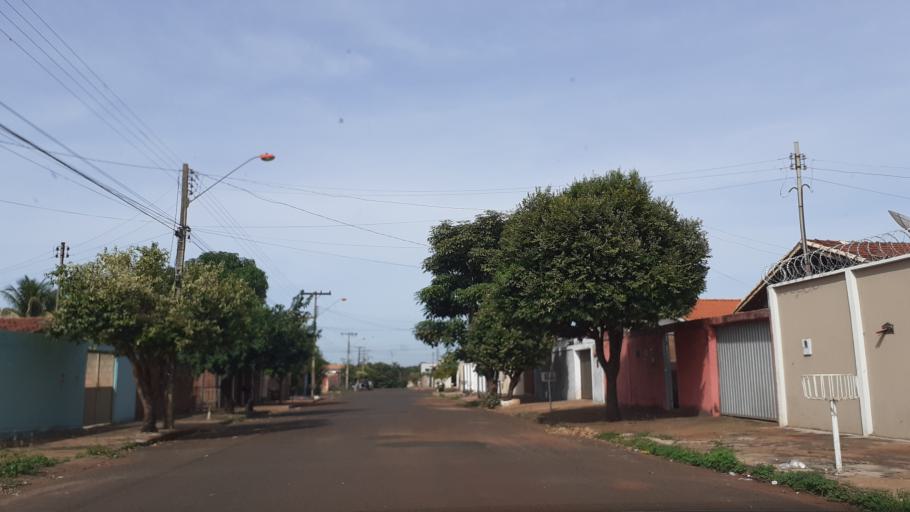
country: BR
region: Goias
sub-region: Itumbiara
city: Itumbiara
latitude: -18.4220
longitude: -49.2420
